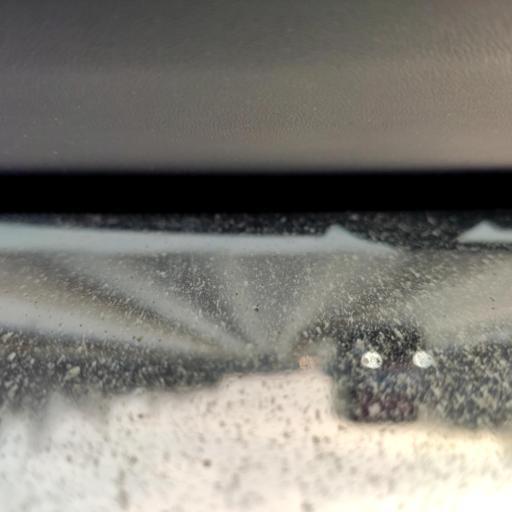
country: RU
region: Perm
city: Krasnokamsk
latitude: 58.0883
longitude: 55.6758
